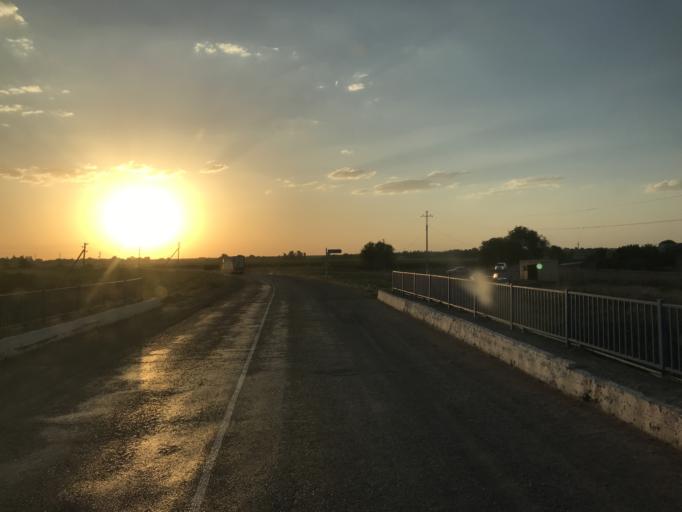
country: UZ
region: Toshkent
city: Yangiyul
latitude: 41.3746
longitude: 68.8261
